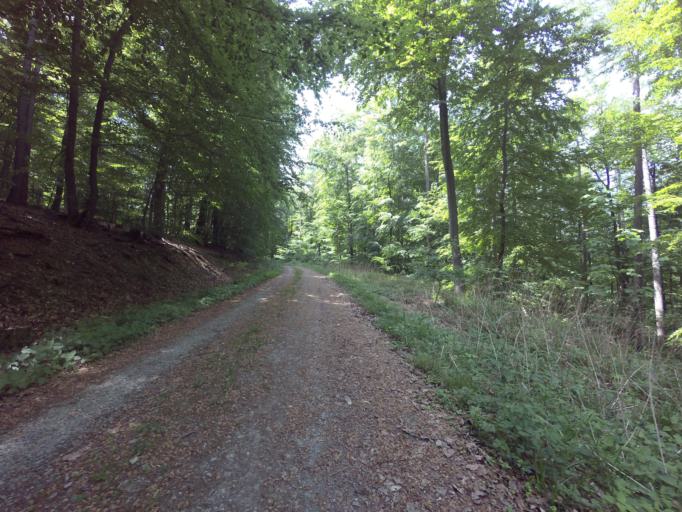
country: DE
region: Lower Saxony
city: Kneitlingen
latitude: 52.1965
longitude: 10.7595
